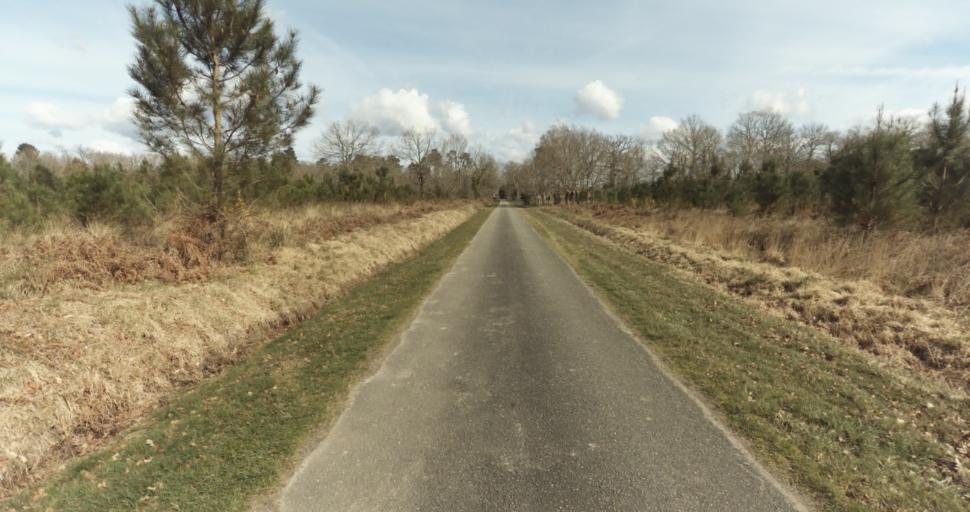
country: FR
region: Aquitaine
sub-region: Departement des Landes
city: Roquefort
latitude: 44.0721
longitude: -0.3306
